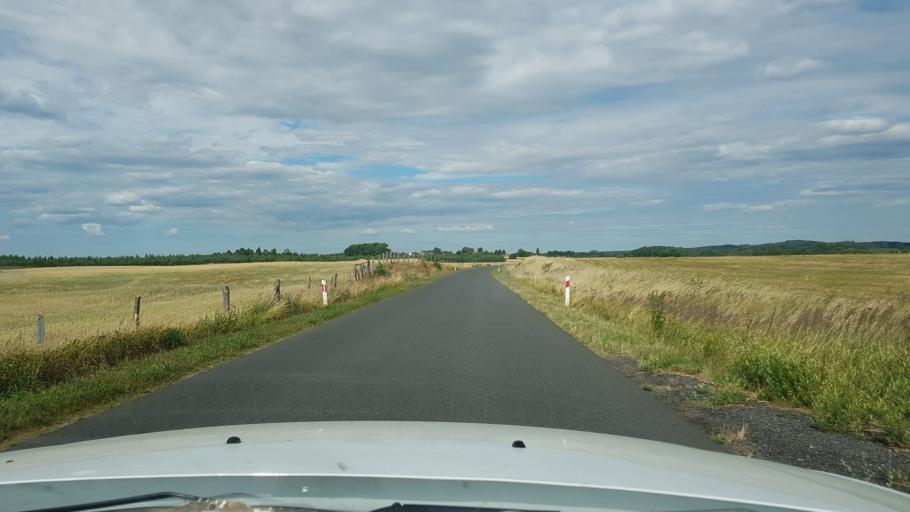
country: PL
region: West Pomeranian Voivodeship
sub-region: Powiat drawski
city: Wierzchowo
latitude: 53.4296
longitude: 16.0582
